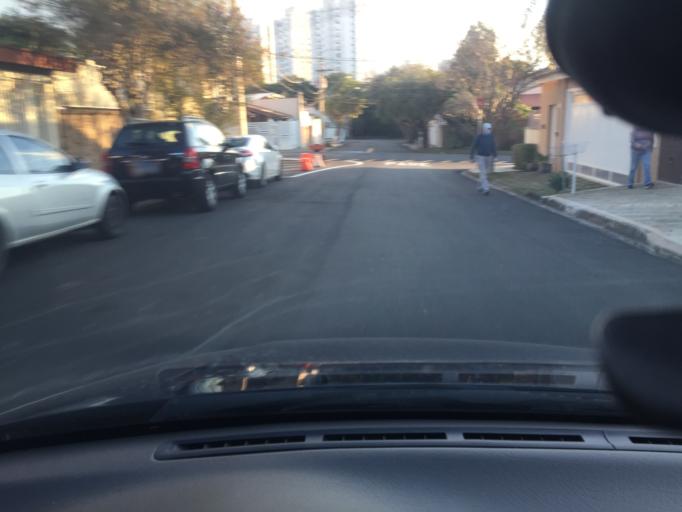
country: BR
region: Sao Paulo
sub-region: Jundiai
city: Jundiai
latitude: -23.1859
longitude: -46.9032
